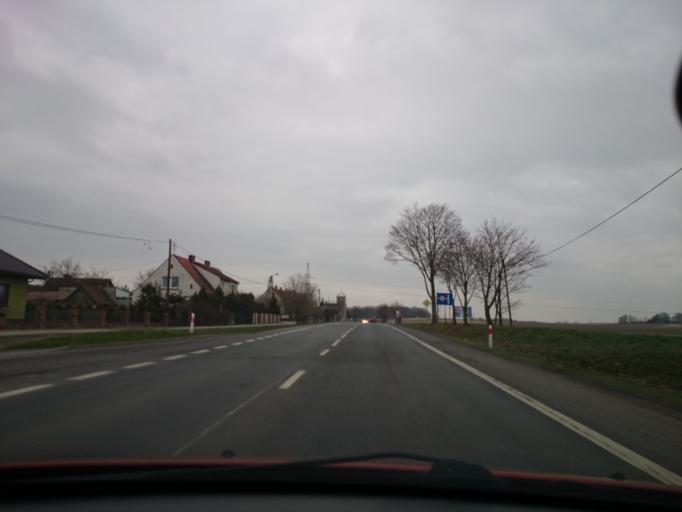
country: PL
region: Opole Voivodeship
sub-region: Powiat opolski
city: Niemodlin
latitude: 50.6390
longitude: 17.6063
